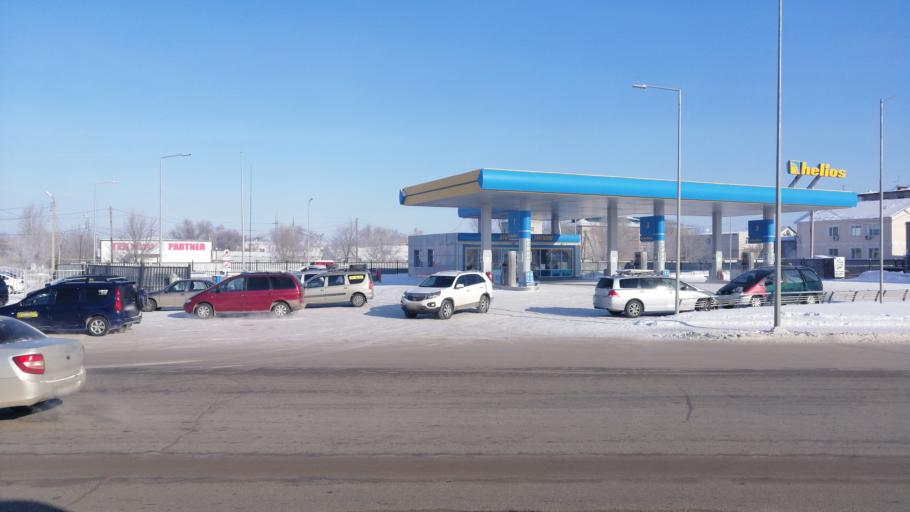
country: KZ
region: Aqtoebe
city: Aqtobe
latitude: 50.2924
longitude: 57.1998
